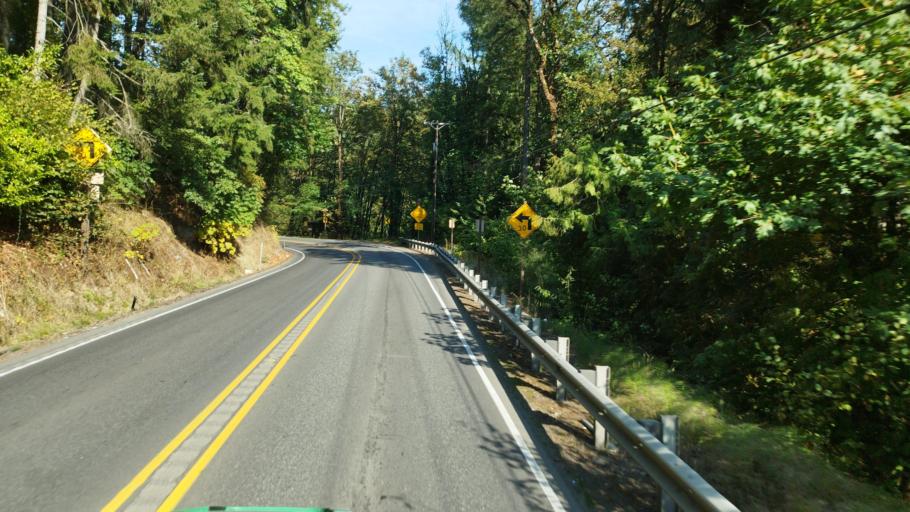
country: US
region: Oregon
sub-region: Washington County
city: Bethany
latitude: 45.6334
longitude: -122.8645
